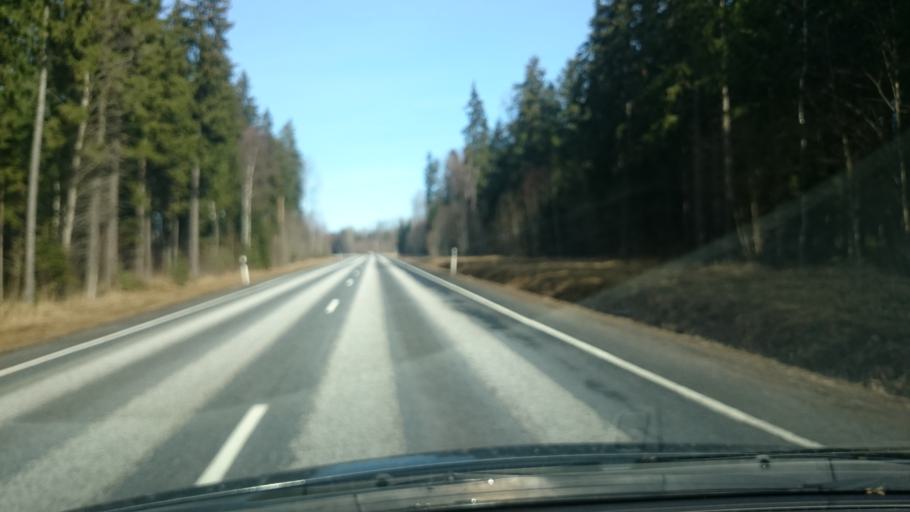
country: EE
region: Jaervamaa
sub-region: Tueri vald
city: Sarevere
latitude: 58.7185
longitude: 25.2760
